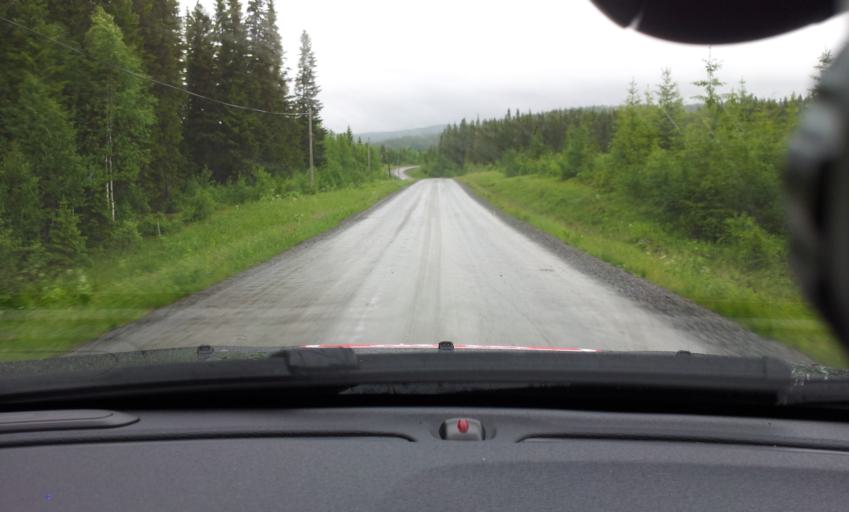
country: SE
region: Jaemtland
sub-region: Are Kommun
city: Are
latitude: 63.4478
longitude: 12.8050
